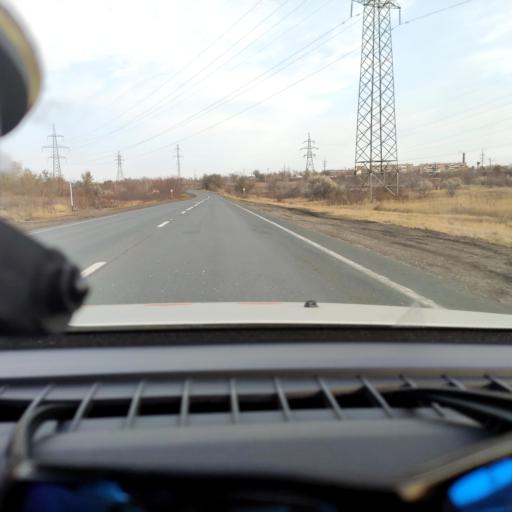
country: RU
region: Samara
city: Chapayevsk
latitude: 52.9871
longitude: 49.7644
